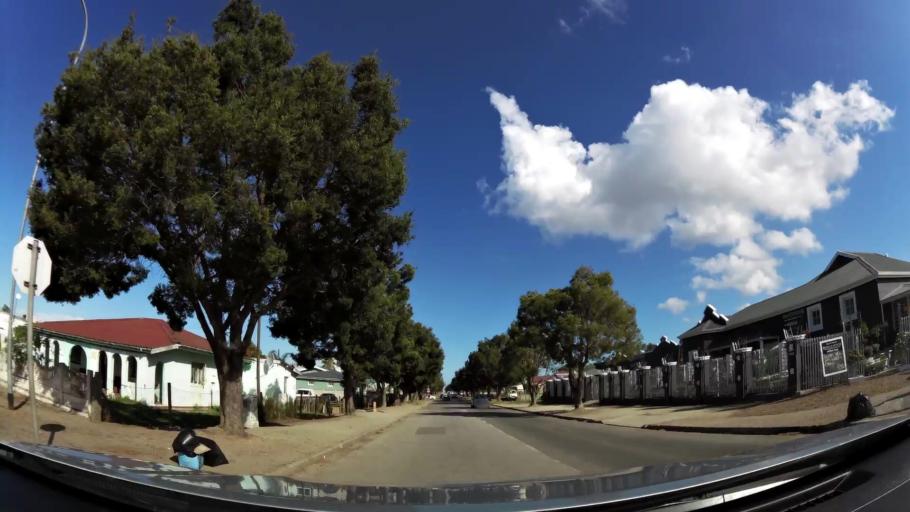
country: ZA
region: Western Cape
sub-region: Eden District Municipality
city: George
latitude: -33.9696
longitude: 22.4635
